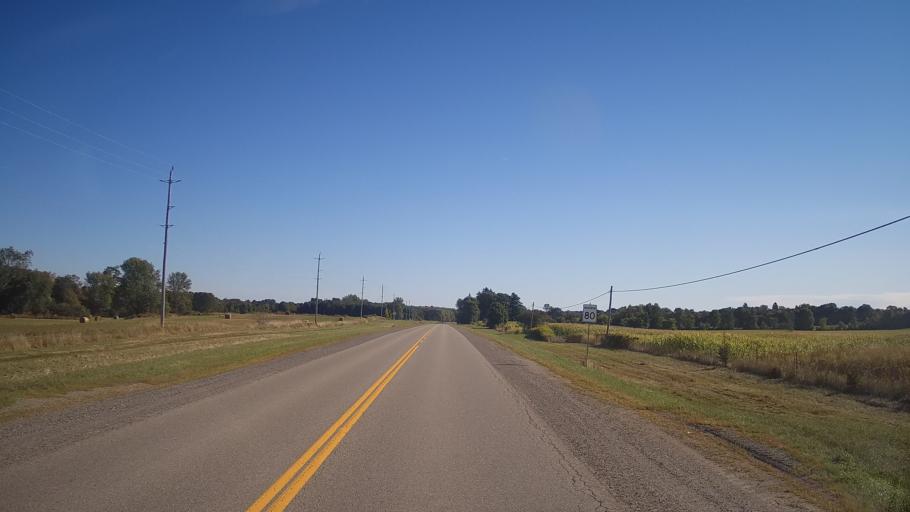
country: CA
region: Ontario
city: Gananoque
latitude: 44.6000
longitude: -76.0809
